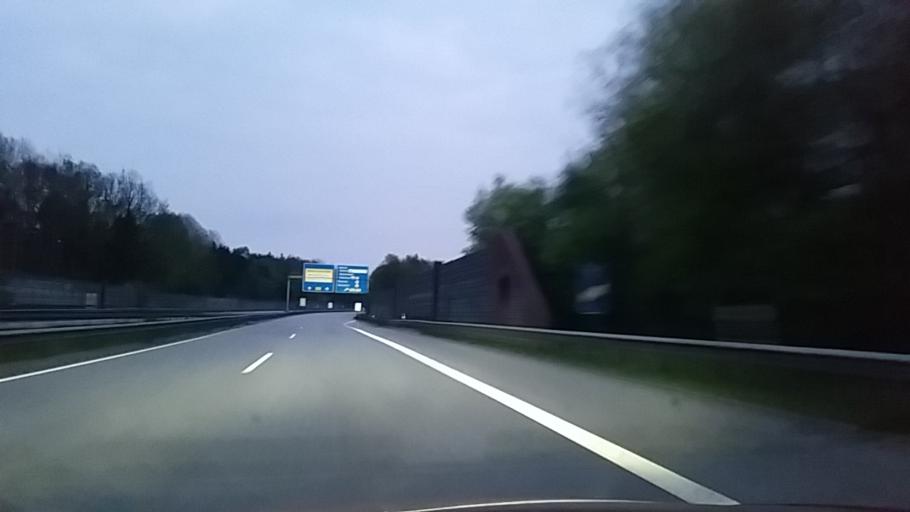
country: DE
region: Schleswig-Holstein
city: Ratekau
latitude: 53.9101
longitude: 10.7694
